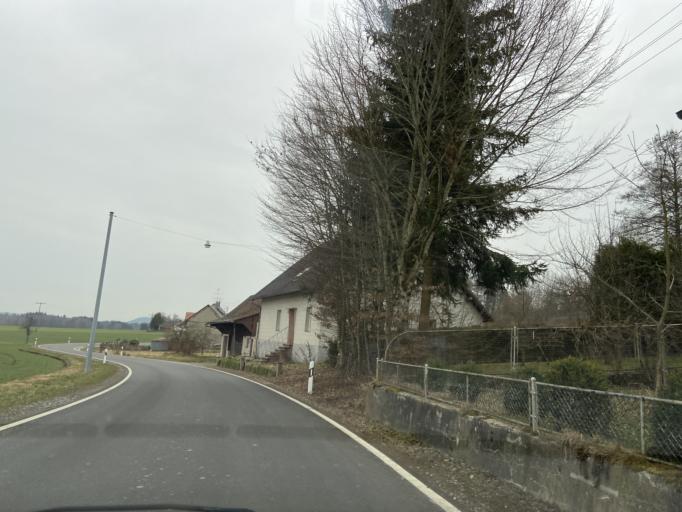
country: DE
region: Baden-Wuerttemberg
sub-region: Tuebingen Region
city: Illmensee
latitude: 47.9042
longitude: 9.3571
